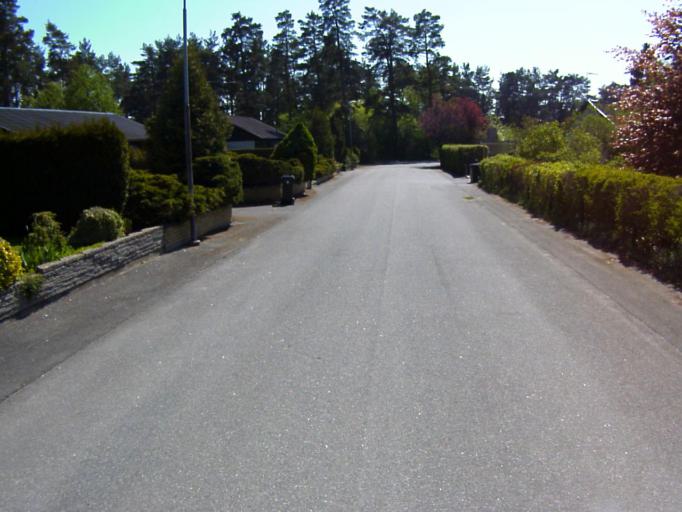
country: SE
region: Skane
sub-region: Kristianstads Kommun
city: Degeberga
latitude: 55.9015
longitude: 14.1009
